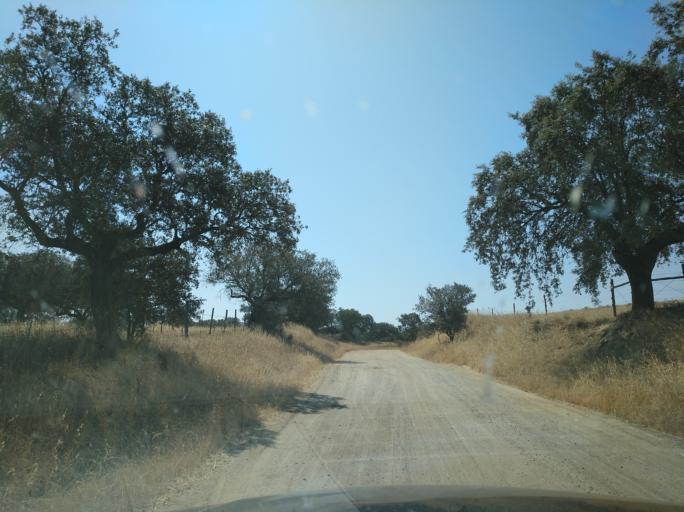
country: PT
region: Portalegre
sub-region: Campo Maior
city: Campo Maior
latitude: 39.0271
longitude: -6.9773
